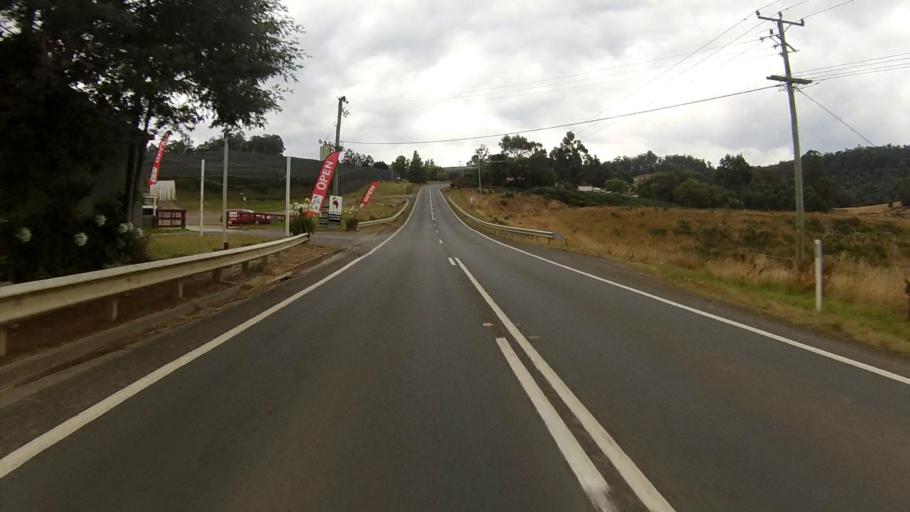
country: AU
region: Tasmania
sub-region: Huon Valley
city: Cygnet
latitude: -43.1321
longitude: 147.0494
